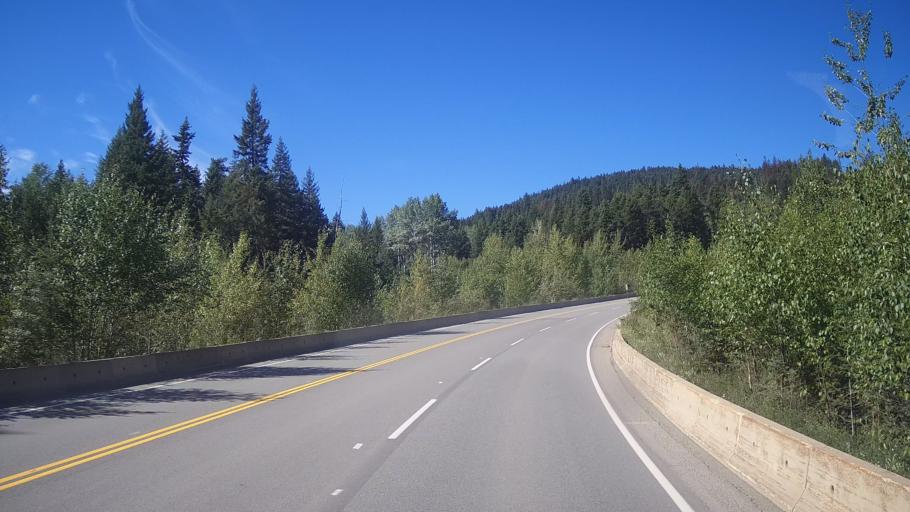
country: CA
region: British Columbia
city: Kamloops
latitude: 51.4631
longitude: -120.2415
